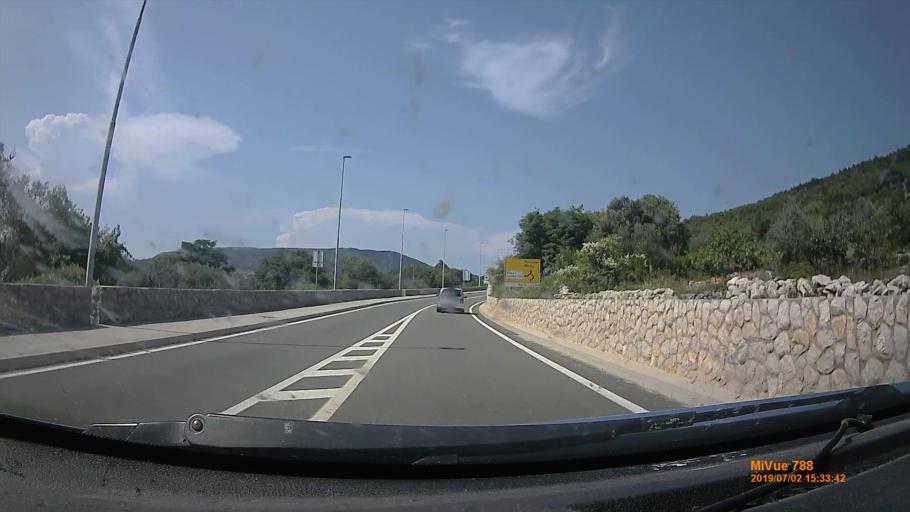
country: HR
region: Primorsko-Goranska
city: Cres
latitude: 44.9616
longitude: 14.4129
